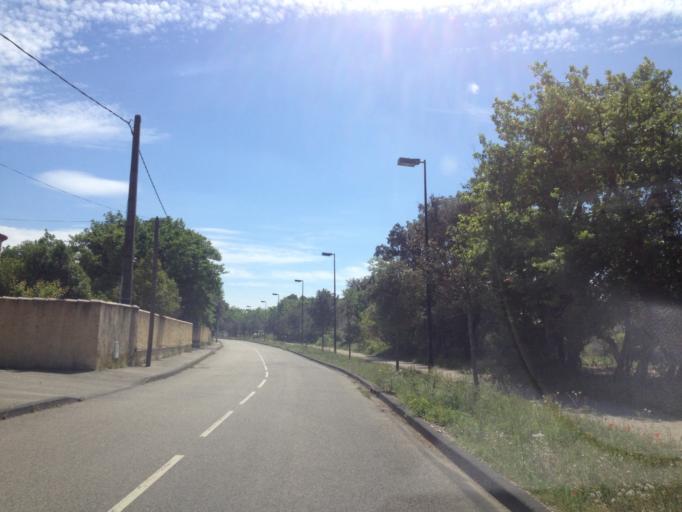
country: FR
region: Provence-Alpes-Cote d'Azur
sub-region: Departement du Vaucluse
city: Orange
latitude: 44.1182
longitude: 4.8222
